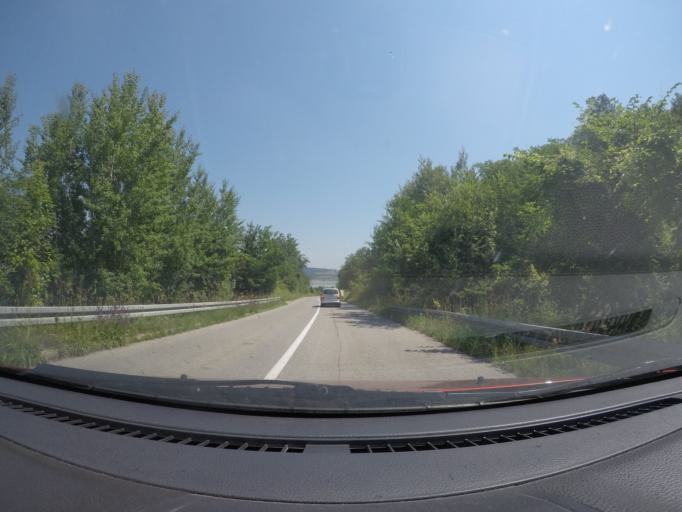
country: RO
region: Mehedinti
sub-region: Comuna Eselnita
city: Eselnita
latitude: 44.6649
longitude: 22.3511
